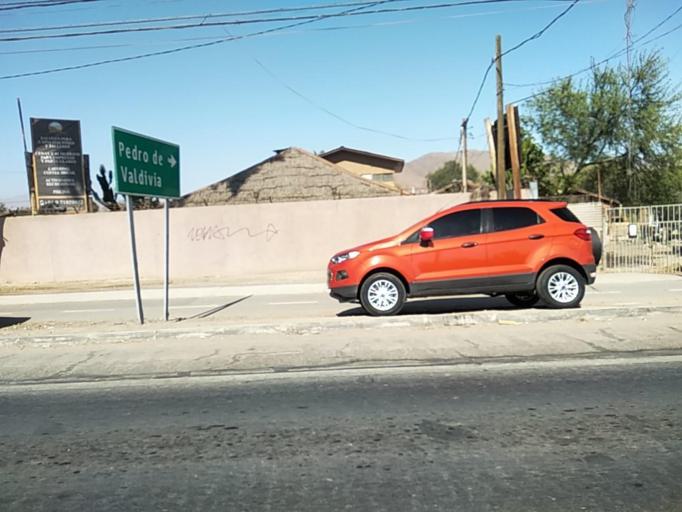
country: CL
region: Atacama
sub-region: Provincia de Copiapo
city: Copiapo
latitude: -27.3911
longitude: -70.3108
